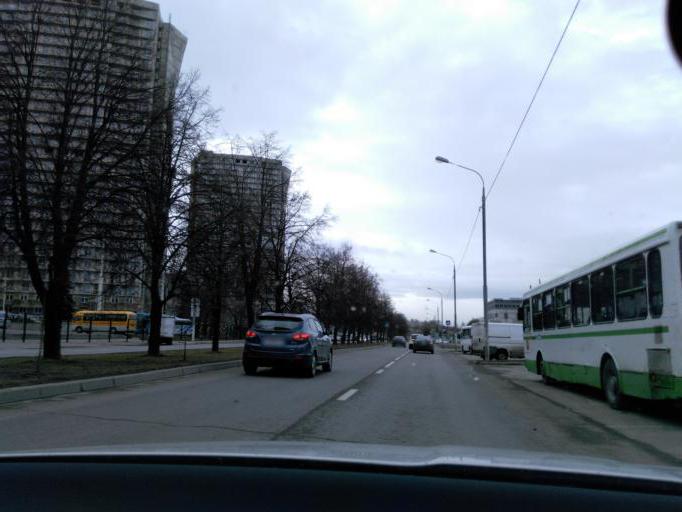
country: RU
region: Moscow
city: Golovinskiy
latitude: 55.8550
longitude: 37.4936
